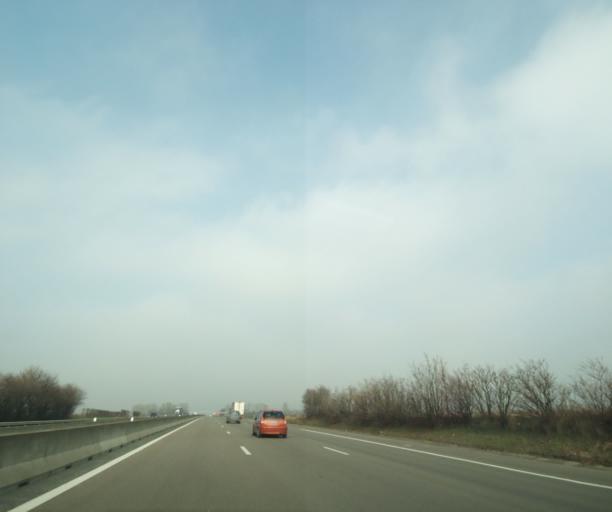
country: FR
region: Rhone-Alpes
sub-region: Departement de l'Isere
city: Auberives-sur-Vareze
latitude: 45.4410
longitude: 4.8262
